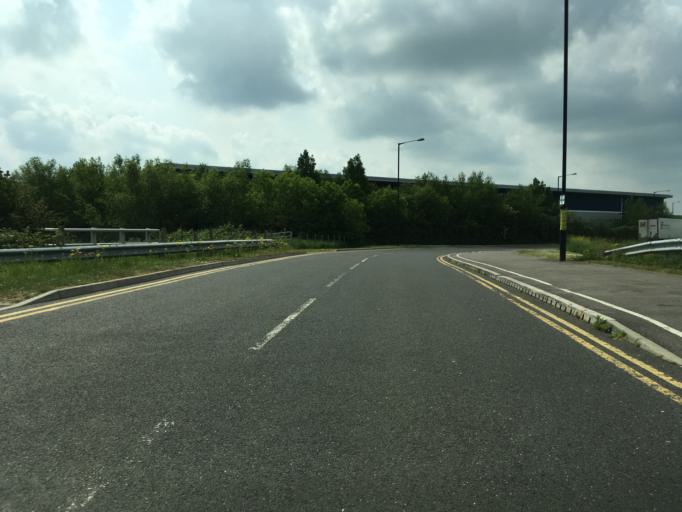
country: GB
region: England
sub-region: South Gloucestershire
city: Severn Beach
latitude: 51.5177
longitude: -2.6669
